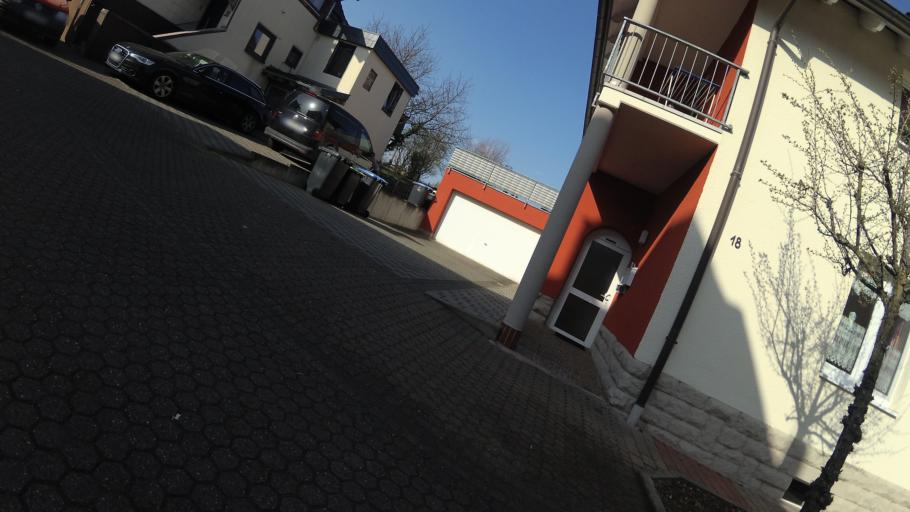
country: DE
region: Saarland
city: Heusweiler
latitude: 49.3302
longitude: 6.9268
